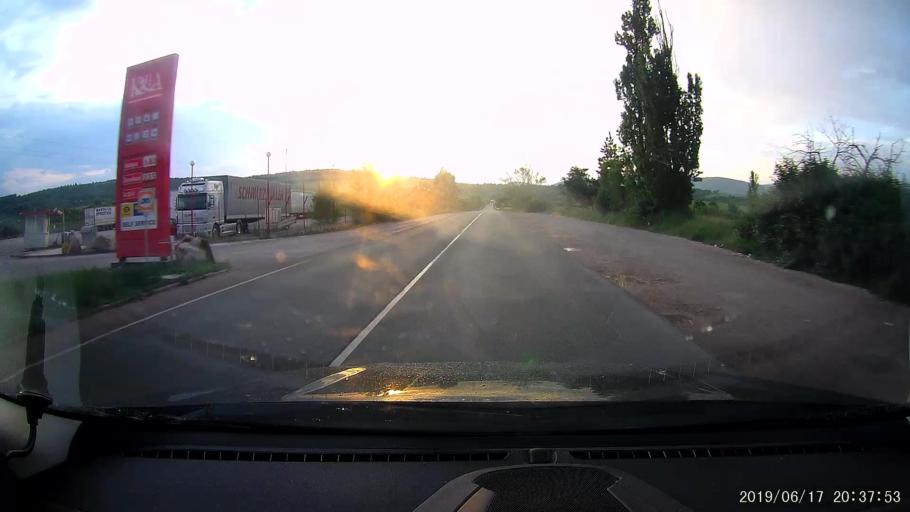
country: BG
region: Sofiya
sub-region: Obshtina Slivnitsa
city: Slivnitsa
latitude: 42.8663
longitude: 23.0255
